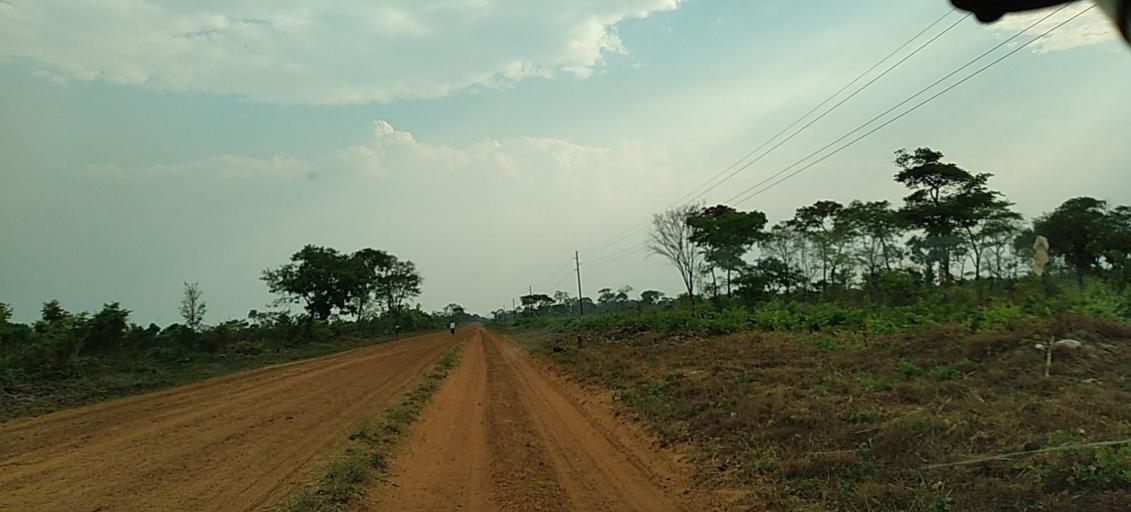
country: ZM
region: North-Western
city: Kabompo
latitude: -13.8905
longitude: 23.6599
